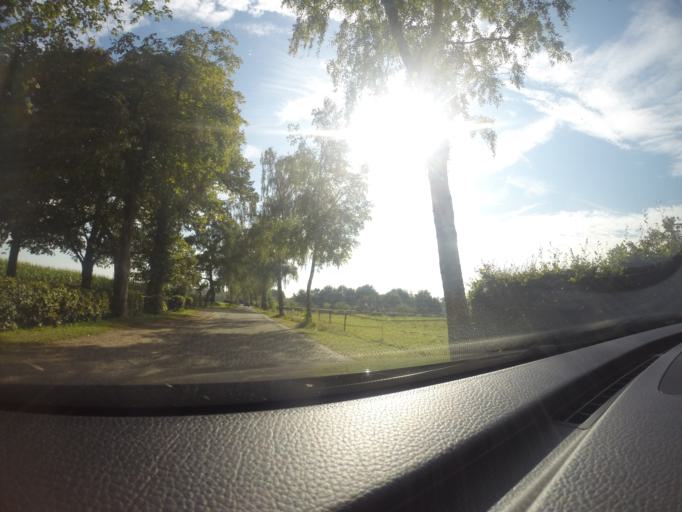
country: NL
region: Gelderland
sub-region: Gemeente Bronckhorst
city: Zelhem
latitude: 51.9737
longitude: 6.3589
